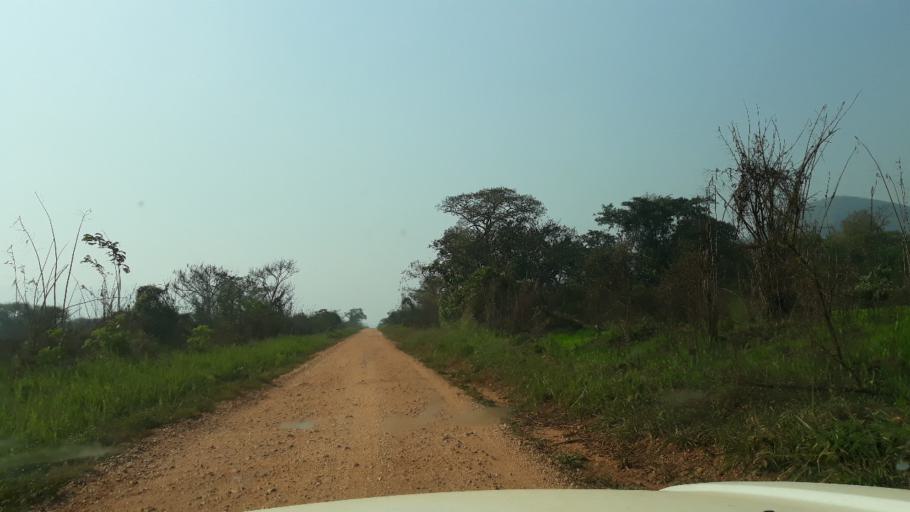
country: BI
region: Bururi
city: Rumonge
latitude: -4.5510
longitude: 28.7904
